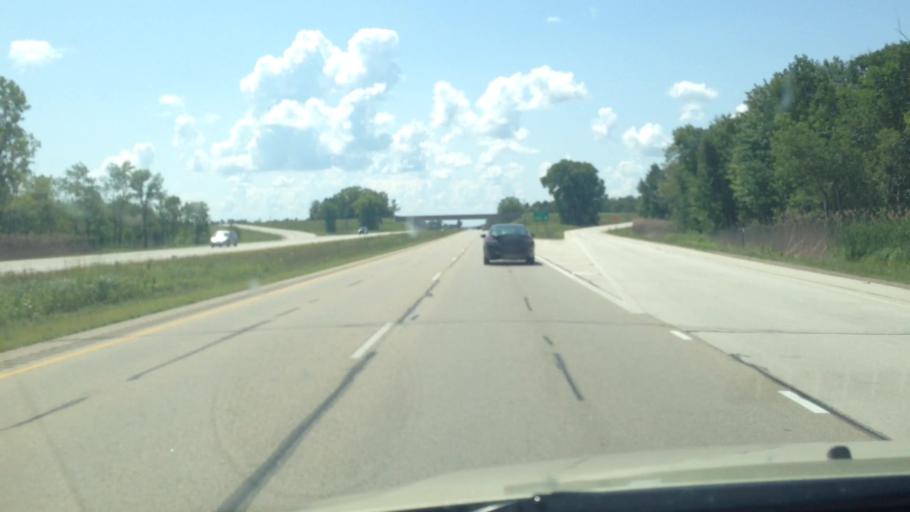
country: US
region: Wisconsin
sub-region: Brown County
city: Suamico
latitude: 44.7256
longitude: -88.0510
